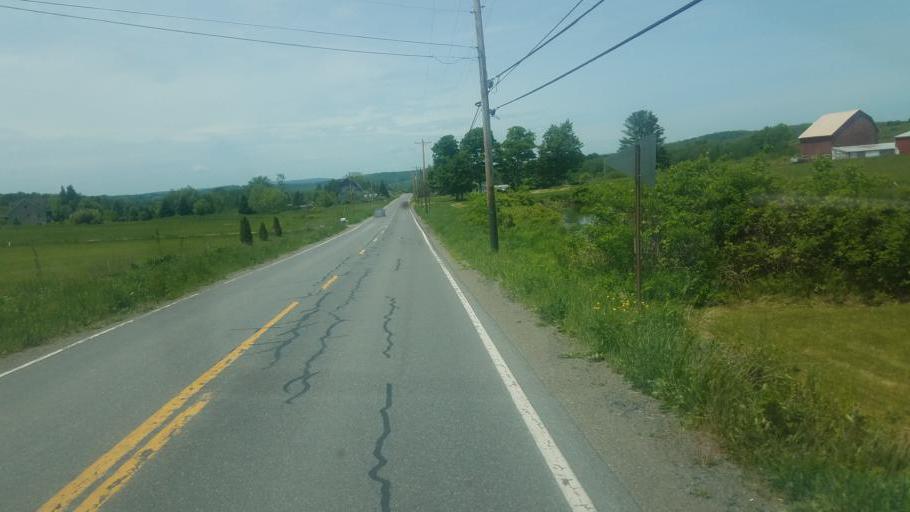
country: US
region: Pennsylvania
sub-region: Tioga County
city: Wellsboro
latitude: 41.7698
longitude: -77.2123
